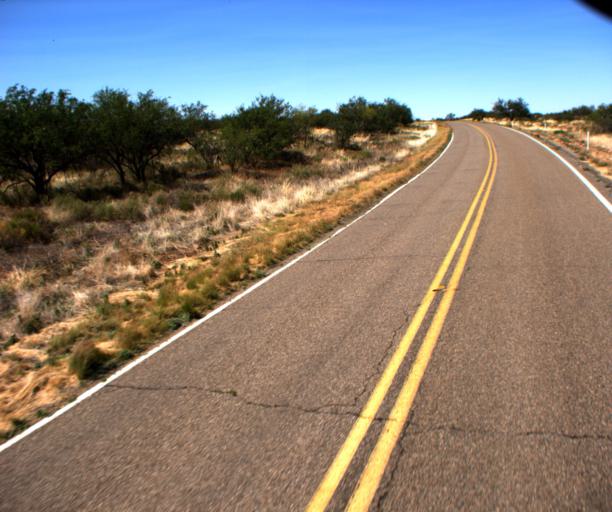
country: US
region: Arizona
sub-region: Pima County
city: Arivaca Junction
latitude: 31.6565
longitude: -111.4931
